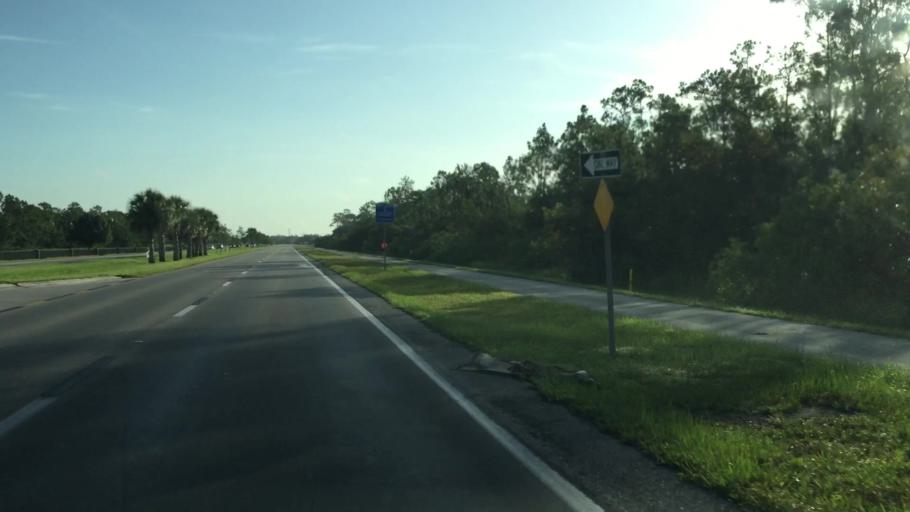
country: US
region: Florida
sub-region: Lee County
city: Fort Myers
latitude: 26.5870
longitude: -81.8184
